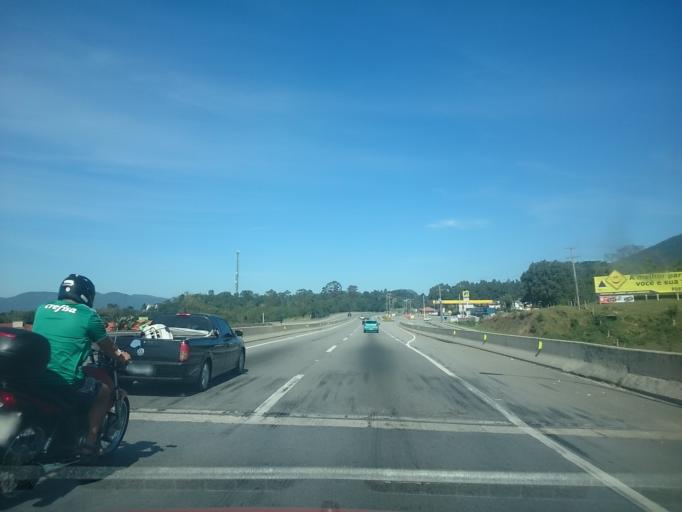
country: BR
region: Santa Catarina
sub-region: Palhoca
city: Palhoca
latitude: -27.7197
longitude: -48.6462
